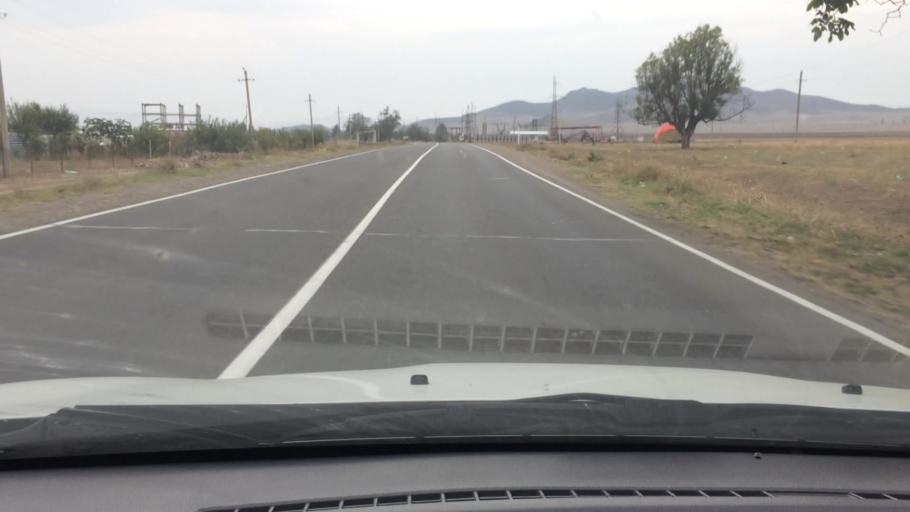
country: GE
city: Naghvarevi
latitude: 41.3937
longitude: 44.8277
